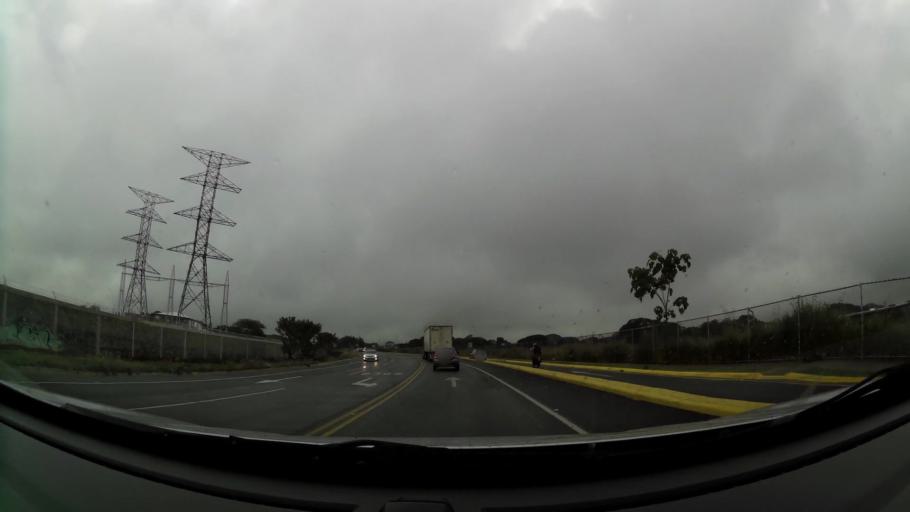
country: CR
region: Alajuela
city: Carrillos
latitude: 9.9911
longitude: -84.2688
